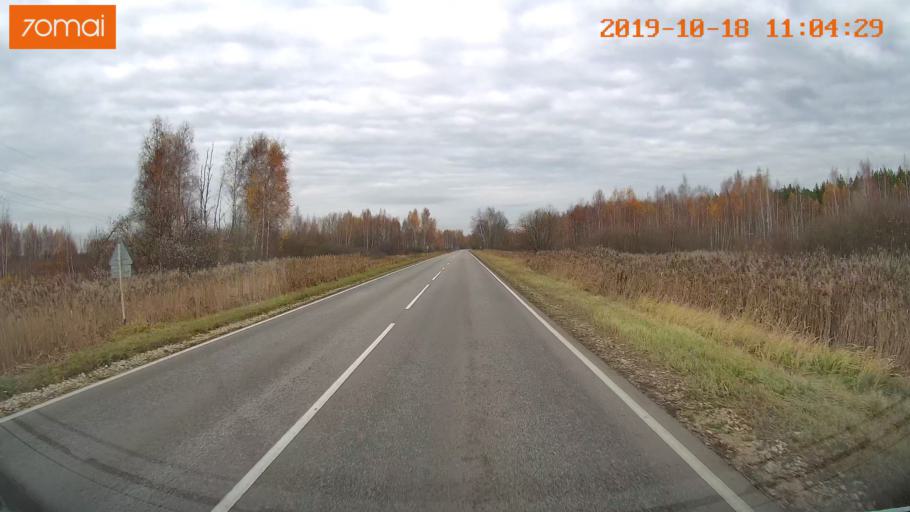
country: RU
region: Tula
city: Yepifan'
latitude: 53.8940
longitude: 38.5470
